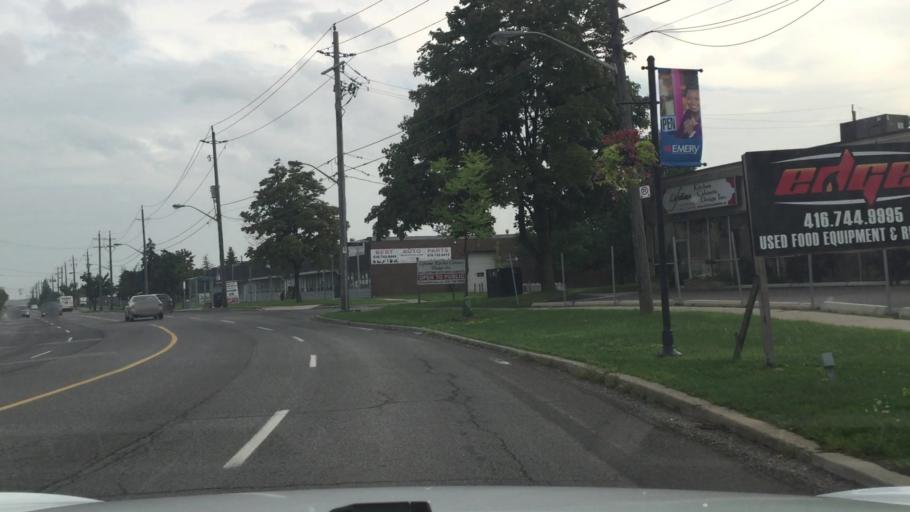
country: CA
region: Ontario
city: Concord
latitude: 43.7423
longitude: -79.5309
